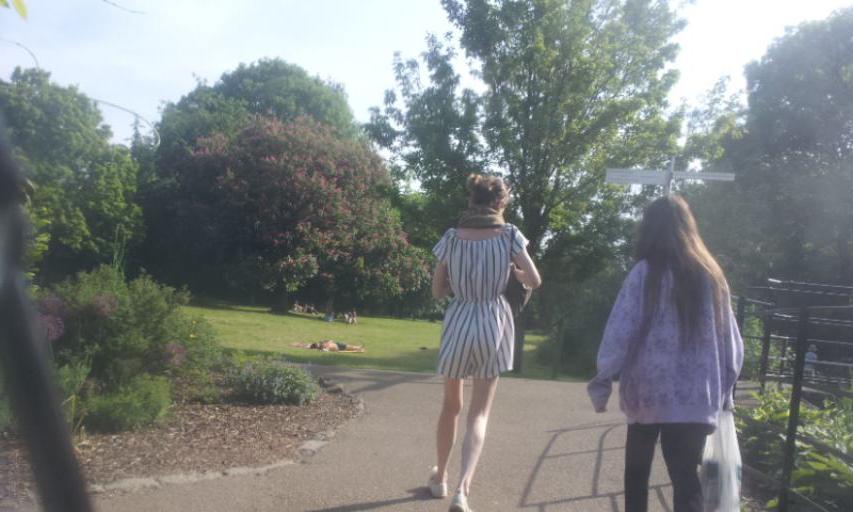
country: GB
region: England
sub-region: Kent
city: Canterbury
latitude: 51.2803
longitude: 1.0735
